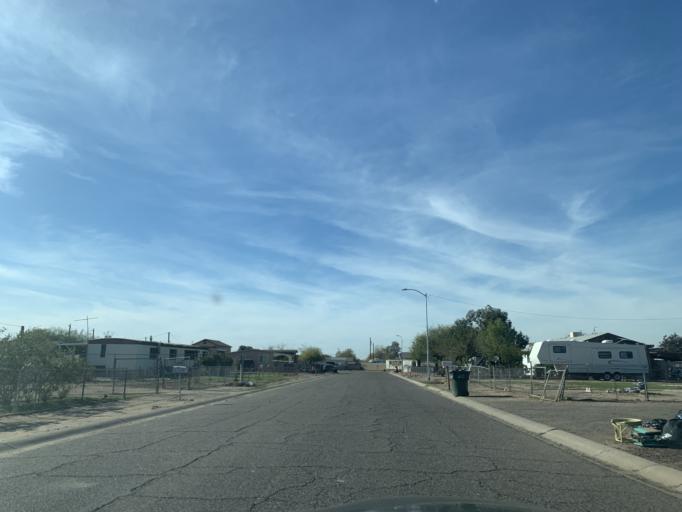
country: US
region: Arizona
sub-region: Maricopa County
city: Laveen
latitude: 33.3950
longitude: -112.1396
